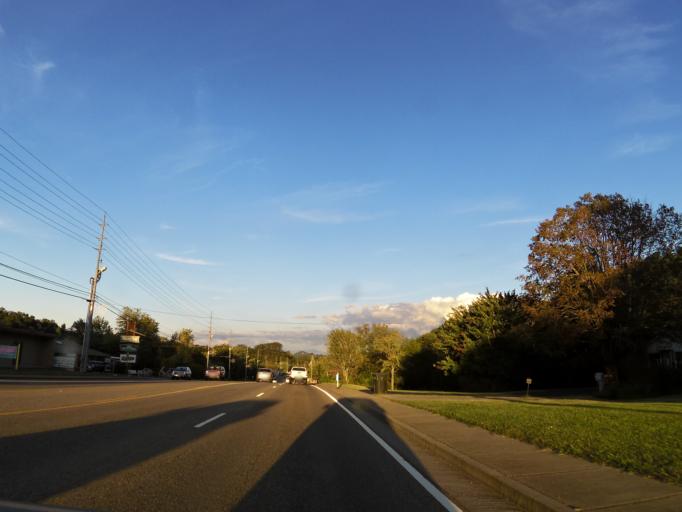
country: US
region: Tennessee
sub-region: Sevier County
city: Pigeon Forge
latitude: 35.7920
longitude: -83.6051
